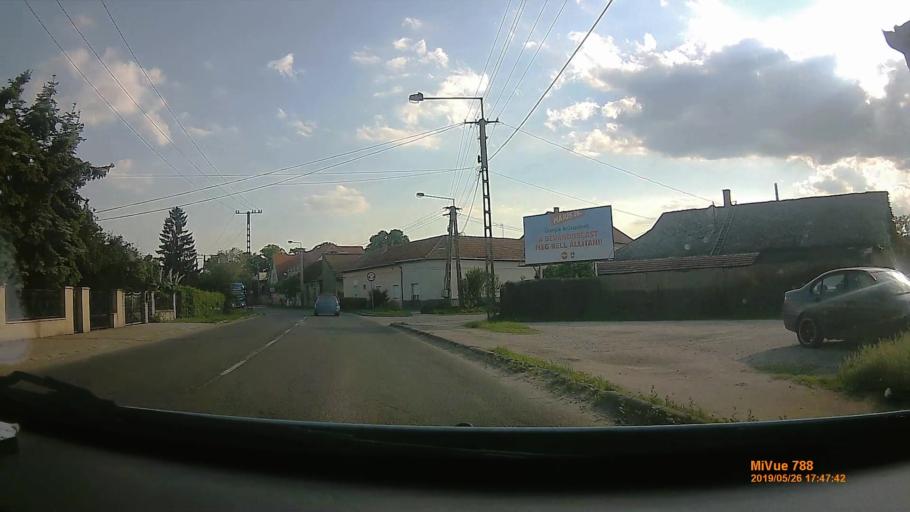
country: HU
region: Borsod-Abauj-Zemplen
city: Szikszo
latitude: 48.2003
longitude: 20.9322
